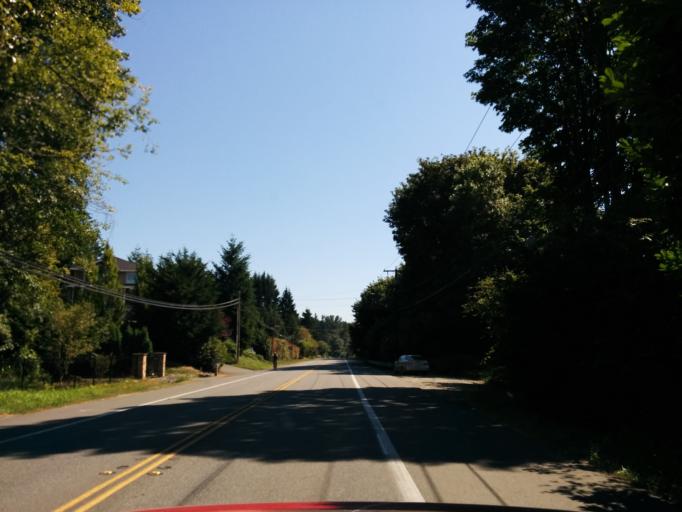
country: US
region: Washington
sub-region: King County
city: Sammamish
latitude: 47.6170
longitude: -122.0677
